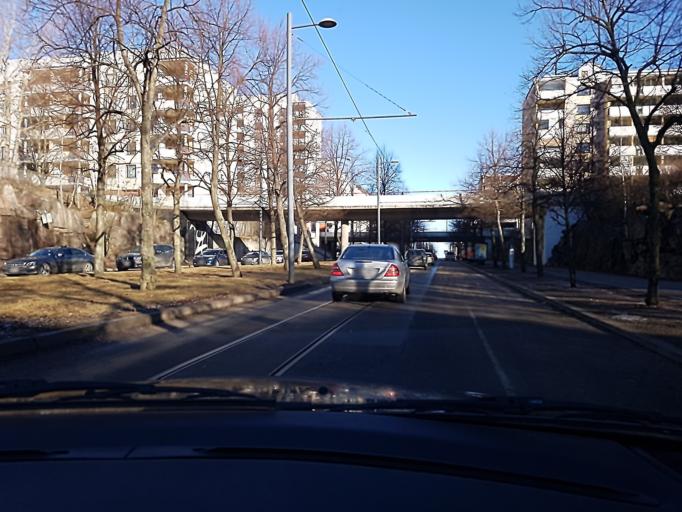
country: FI
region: Uusimaa
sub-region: Helsinki
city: Helsinki
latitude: 60.1968
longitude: 24.9413
